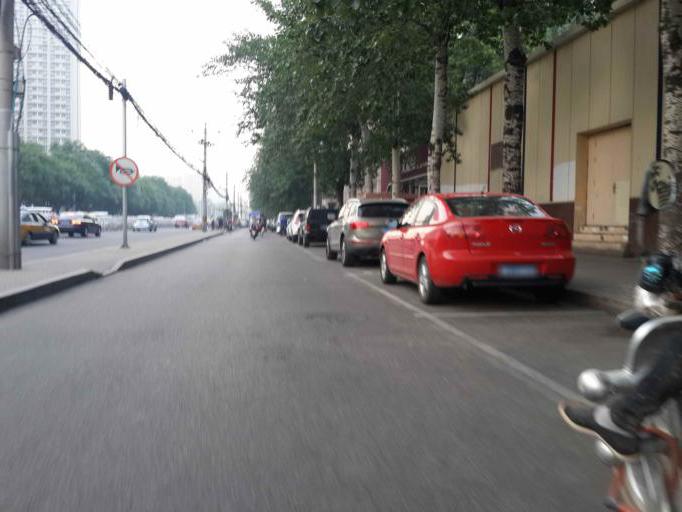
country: CN
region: Beijing
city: Chaowai
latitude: 39.9331
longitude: 116.4444
